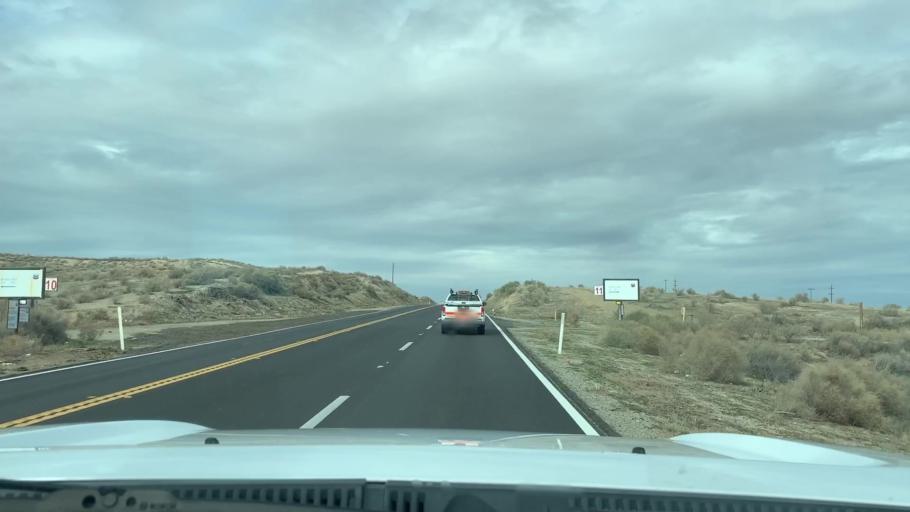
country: US
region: California
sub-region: Kern County
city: South Taft
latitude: 35.1171
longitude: -119.4314
